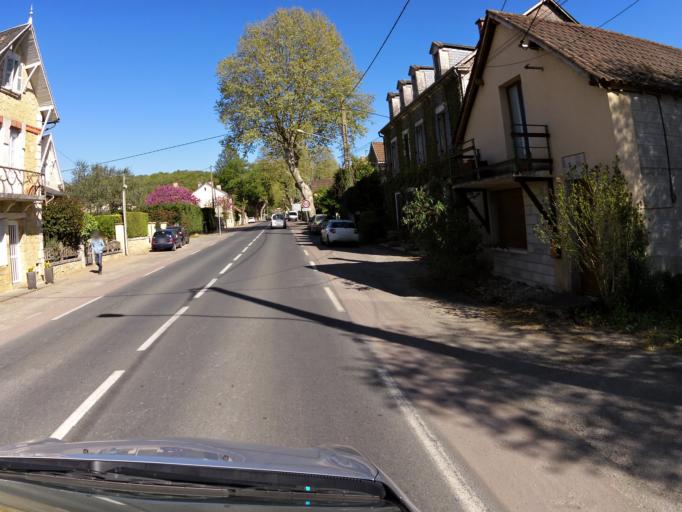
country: FR
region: Aquitaine
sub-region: Departement de la Dordogne
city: Montignac
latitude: 45.0648
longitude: 1.1702
